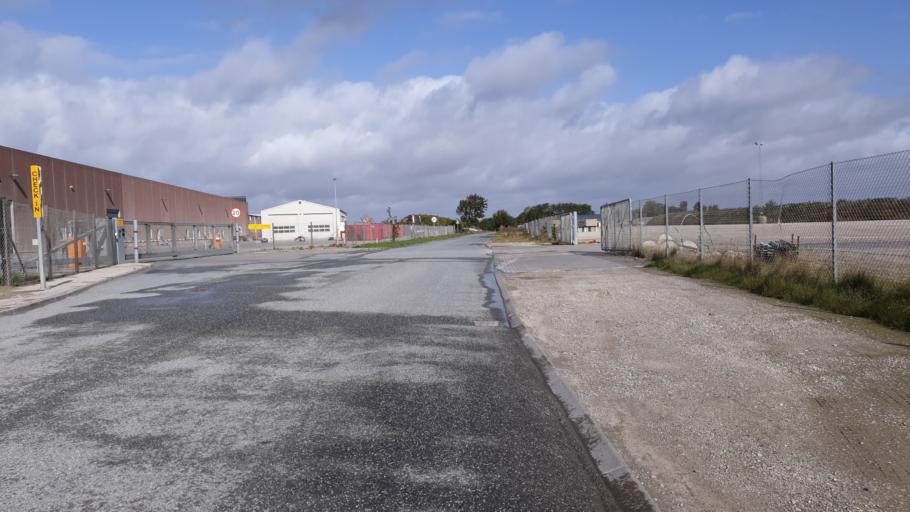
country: DK
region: Central Jutland
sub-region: Hedensted Kommune
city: Hedensted
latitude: 55.8099
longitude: 9.6858
